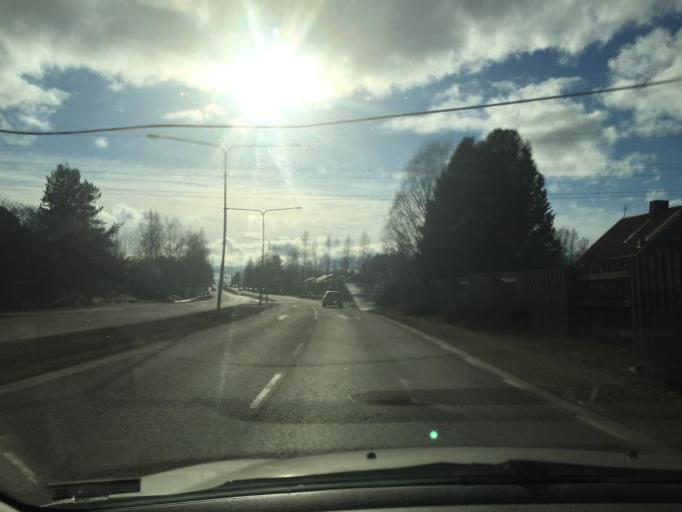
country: SE
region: Norrbotten
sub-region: Lulea Kommun
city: Lulea
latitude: 65.5847
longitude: 22.2162
